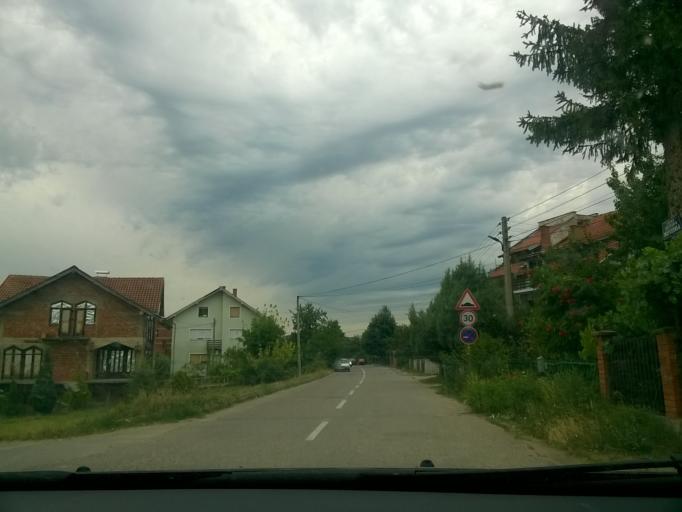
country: RS
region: Central Serbia
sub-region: Zajecarski Okrug
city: Soko Banja
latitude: 43.6480
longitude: 21.8816
